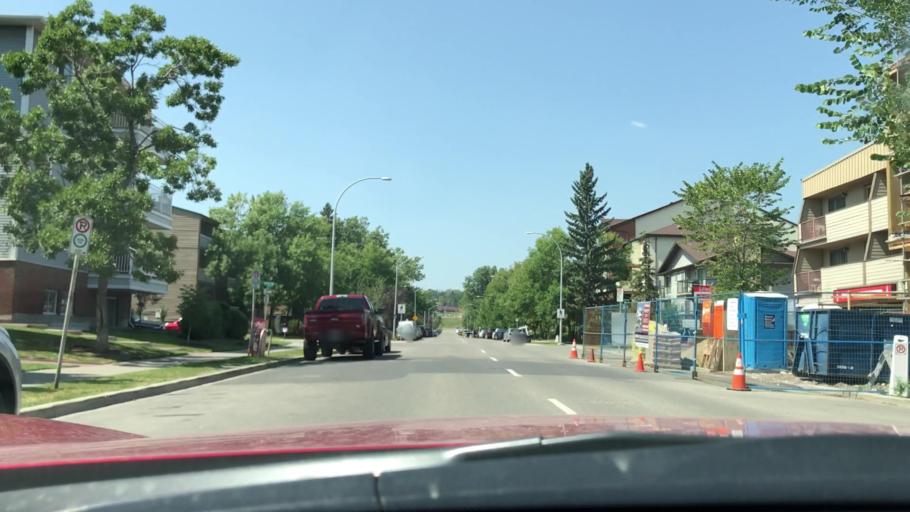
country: CA
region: Alberta
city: Calgary
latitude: 51.0434
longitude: -114.1010
